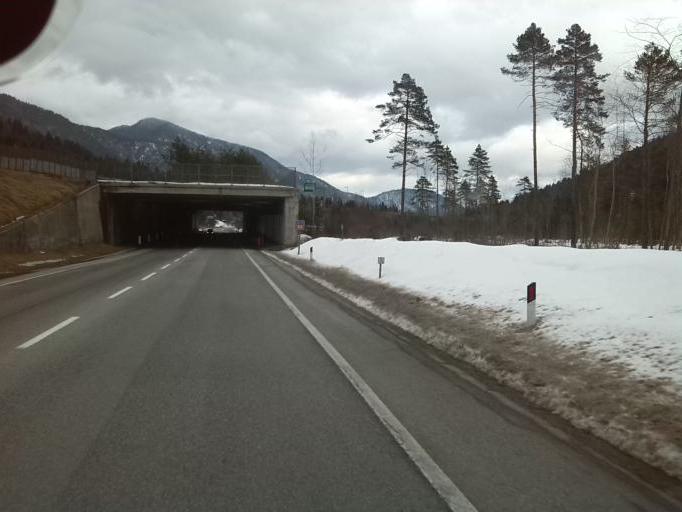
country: IT
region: Friuli Venezia Giulia
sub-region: Provincia di Udine
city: Malborghetto
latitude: 46.5043
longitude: 13.5114
